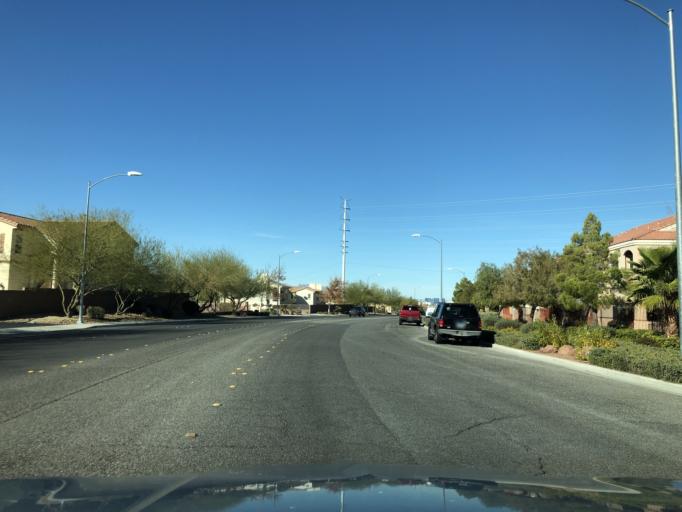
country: US
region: Nevada
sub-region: Clark County
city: Whitney
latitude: 36.0011
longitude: -115.0938
